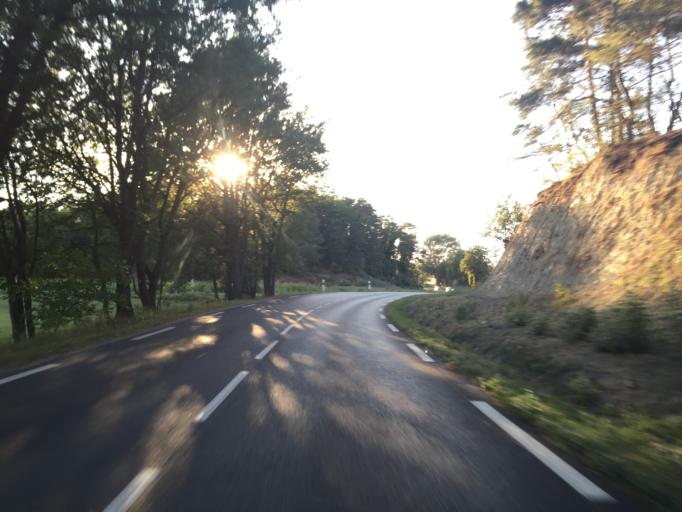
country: FR
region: Provence-Alpes-Cote d'Azur
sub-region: Departement des Alpes-de-Haute-Provence
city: Reillanne
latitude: 43.8588
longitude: 5.6401
